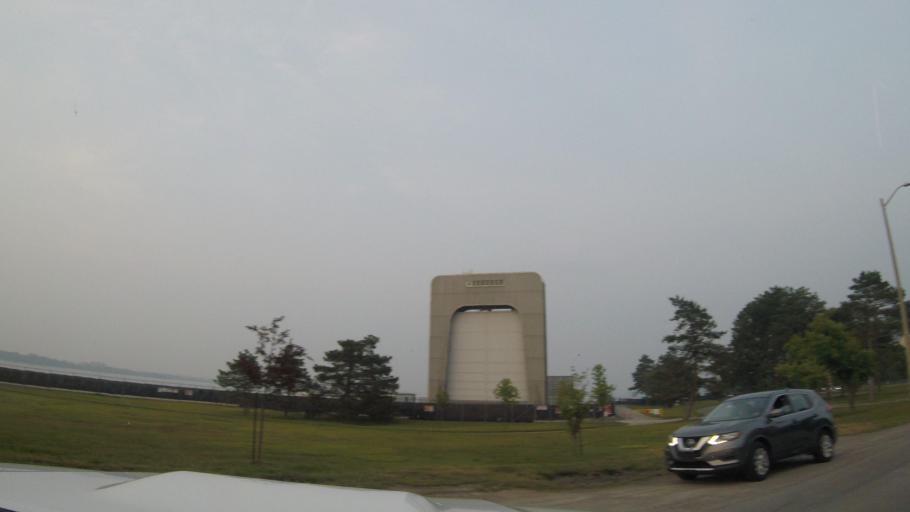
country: US
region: New York
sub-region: Niagara County
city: Niagara Falls
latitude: 43.0662
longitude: -79.0540
